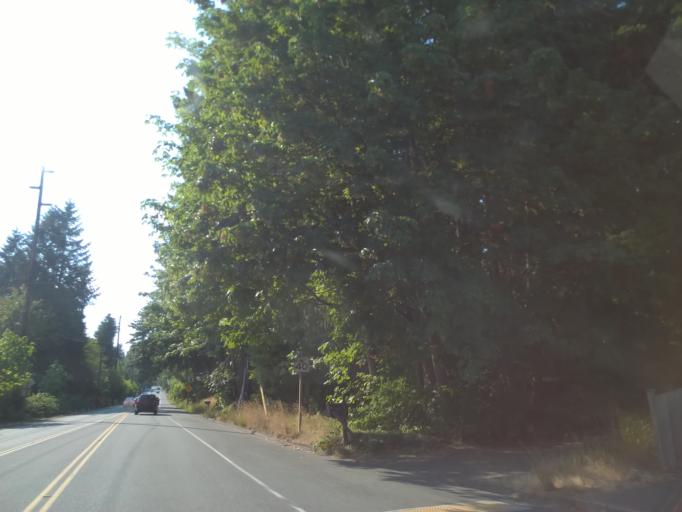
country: US
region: Washington
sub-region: King County
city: Cottage Lake
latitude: 47.7562
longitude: -122.0835
